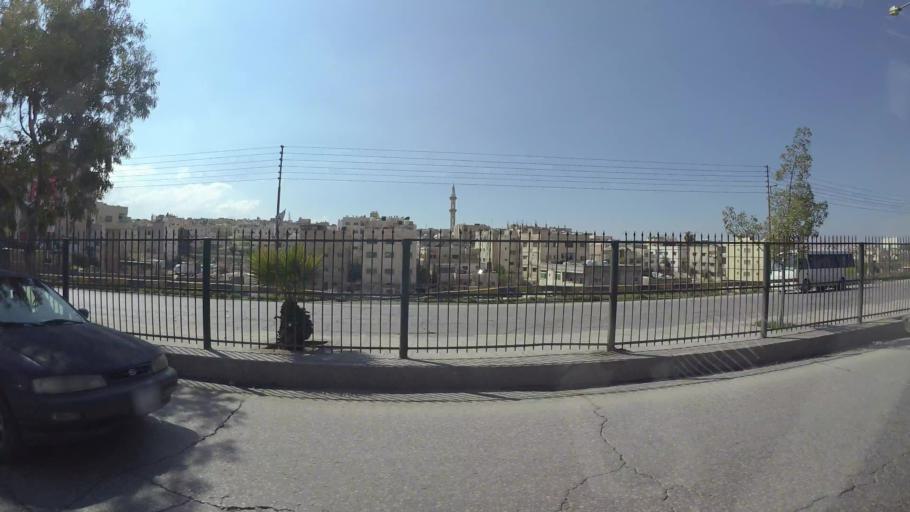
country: JO
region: Zarqa
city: Zarqa
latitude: 32.0428
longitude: 36.0942
